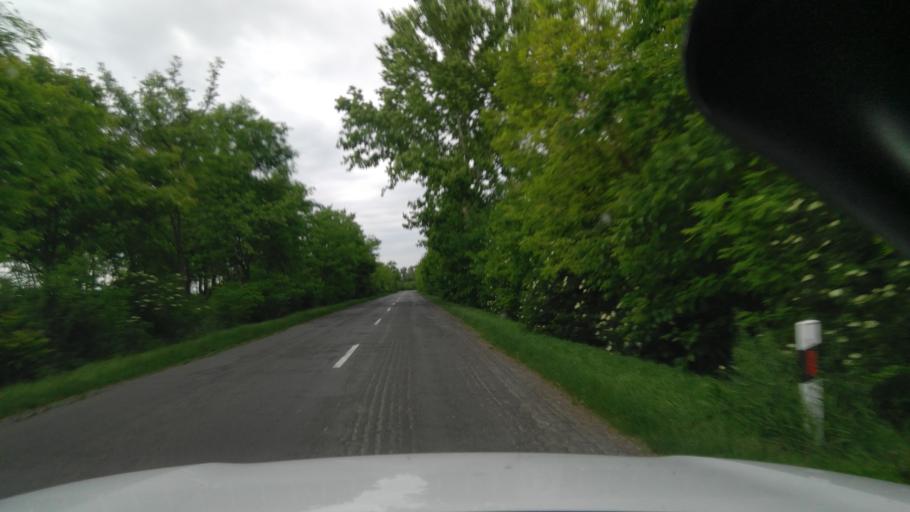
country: HU
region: Bekes
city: Bekescsaba
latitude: 46.6820
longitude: 21.1668
